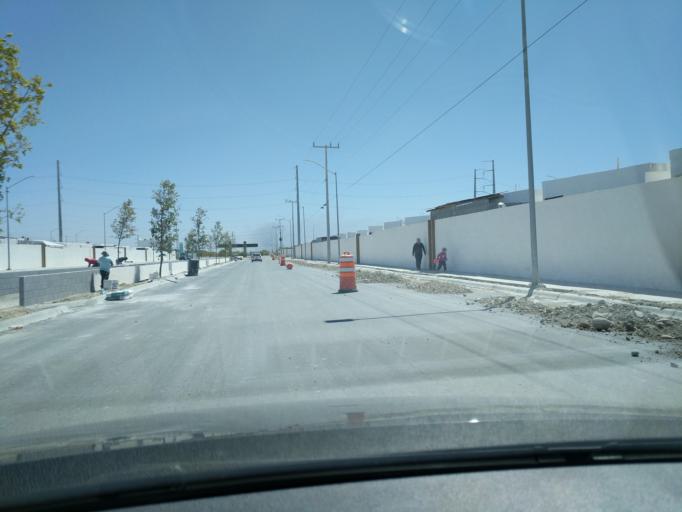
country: MX
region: Nuevo Leon
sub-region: Apodaca
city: Artemio Trevino
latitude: 25.8422
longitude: -100.1392
